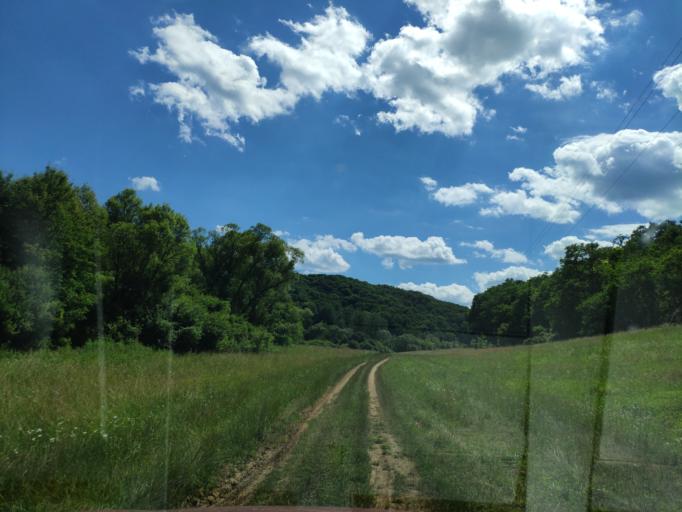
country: HU
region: Borsod-Abauj-Zemplen
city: Arlo
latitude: 48.2612
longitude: 20.1884
